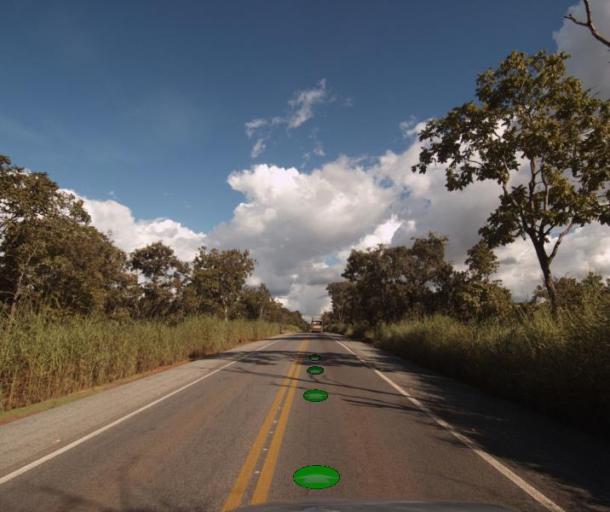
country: BR
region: Goias
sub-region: Porangatu
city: Porangatu
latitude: -13.1655
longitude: -49.1759
